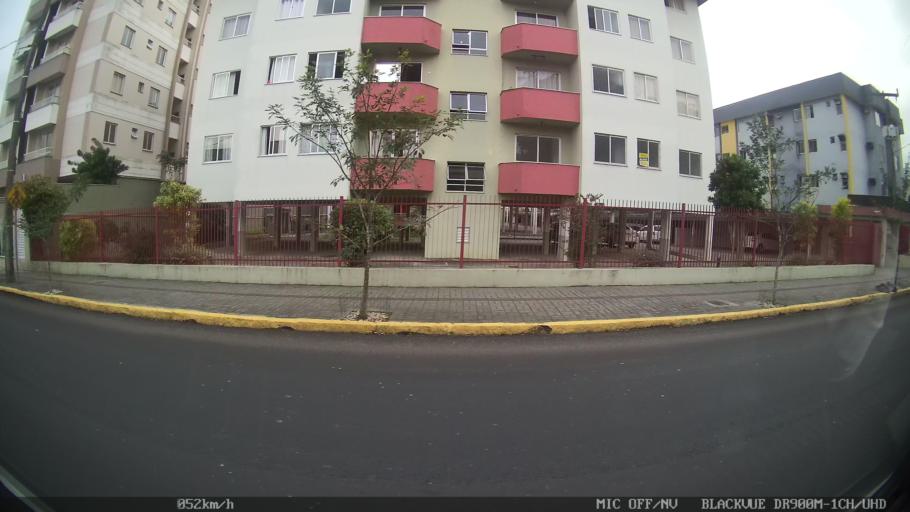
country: BR
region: Santa Catarina
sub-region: Joinville
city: Joinville
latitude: -26.2908
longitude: -48.8679
